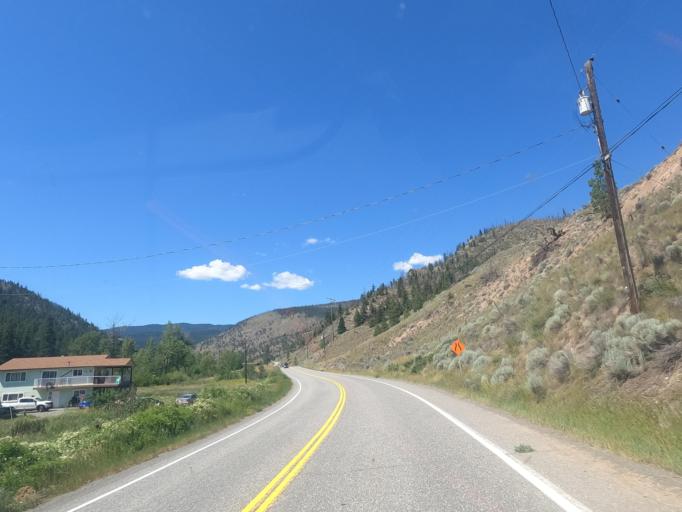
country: CA
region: British Columbia
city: Cache Creek
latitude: 50.8852
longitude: -121.4847
